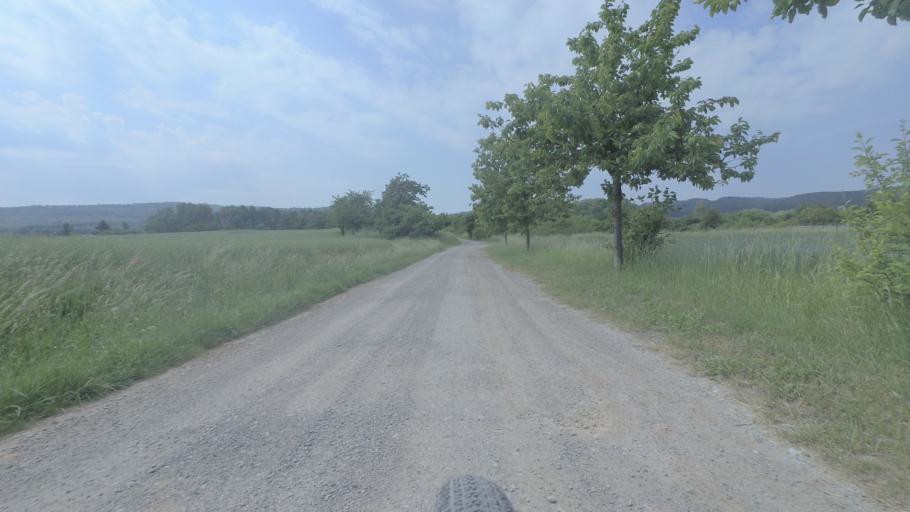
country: DE
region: Saxony-Anhalt
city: Blankenburg
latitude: 51.7700
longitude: 10.9703
